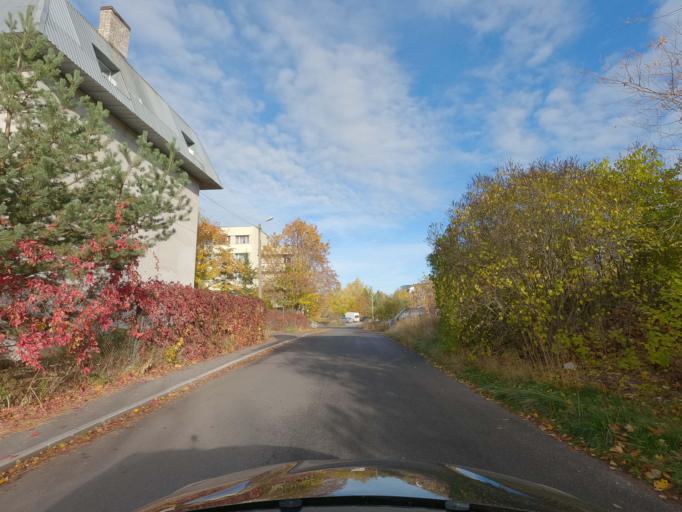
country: EE
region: Harju
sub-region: Tallinna linn
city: Tallinn
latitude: 59.3971
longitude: 24.7158
